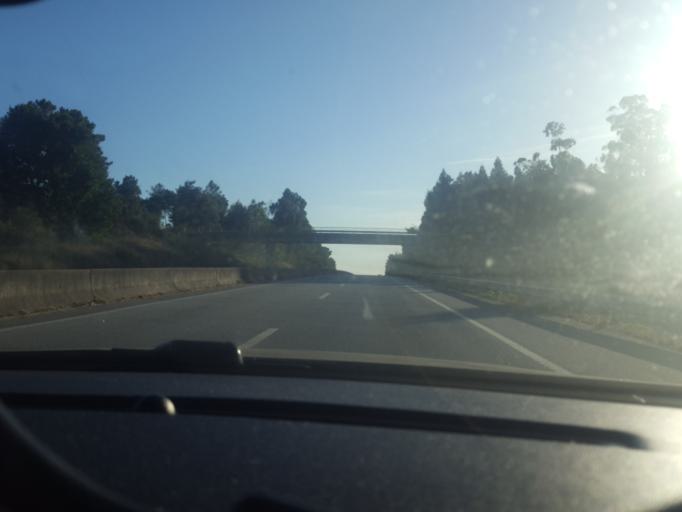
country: PT
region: Viseu
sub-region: Concelho de Carregal do Sal
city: Carregal do Sal
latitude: 40.4678
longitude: -7.9403
